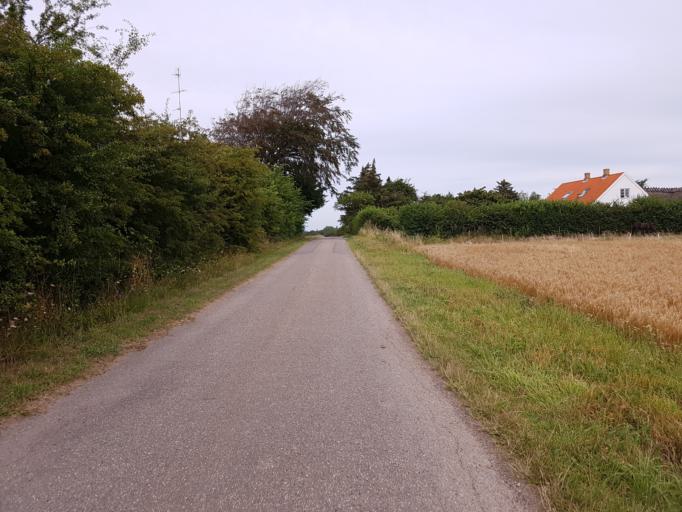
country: DK
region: Zealand
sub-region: Guldborgsund Kommune
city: Nykobing Falster
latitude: 54.5971
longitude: 11.9297
